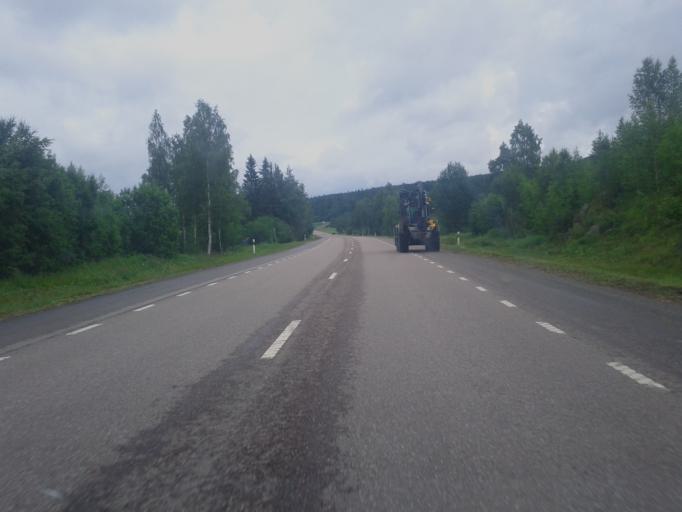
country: SE
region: Vaesternorrland
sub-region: Sundsvalls Kommun
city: Vi
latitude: 62.3784
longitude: 17.1470
